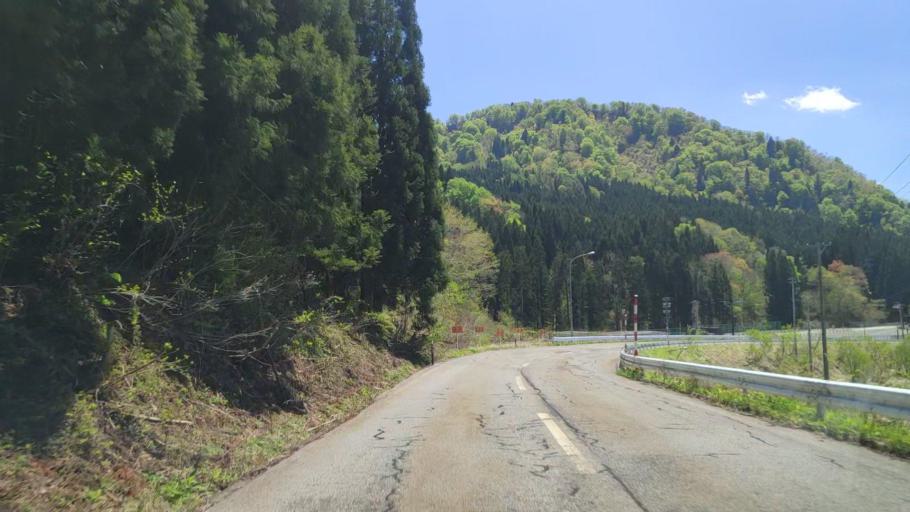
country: JP
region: Yamagata
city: Shinjo
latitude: 38.9543
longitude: 140.3587
